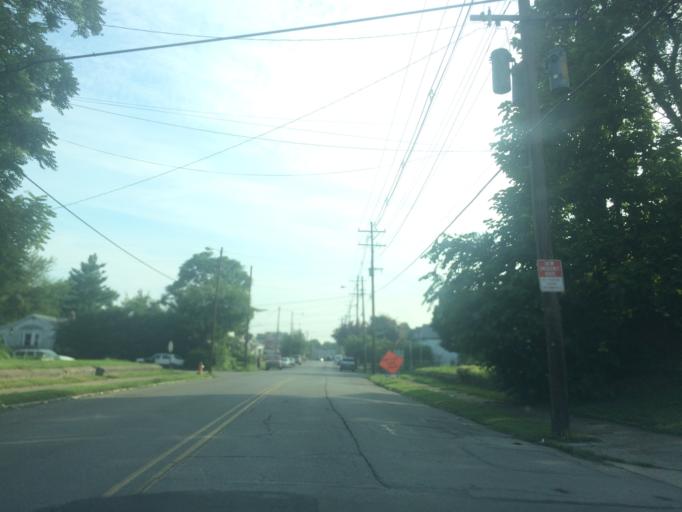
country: US
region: Kentucky
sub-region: Jefferson County
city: Audubon Park
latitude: 38.2226
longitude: -85.7432
